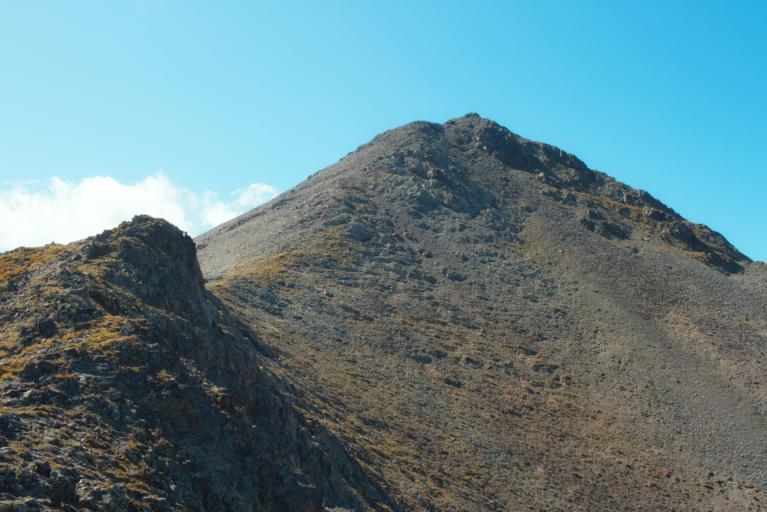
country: RU
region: Karachayevo-Cherkesiya
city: Mednogorskiy
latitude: 43.6193
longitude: 41.0943
